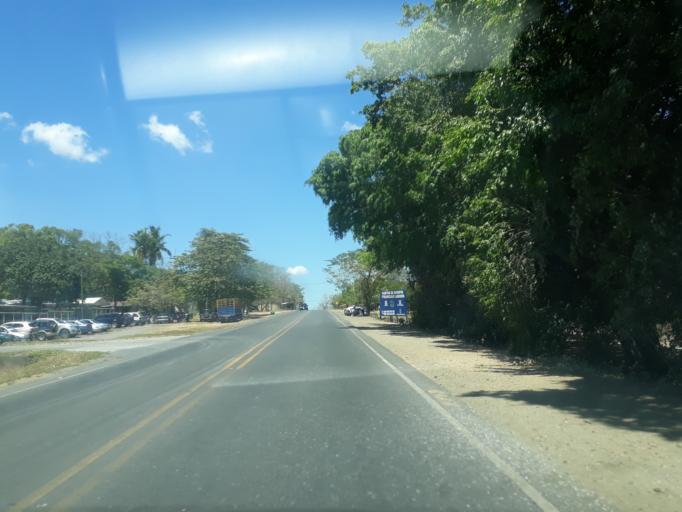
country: CR
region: Guanacaste
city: Liberia
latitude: 10.6620
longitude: -85.4711
